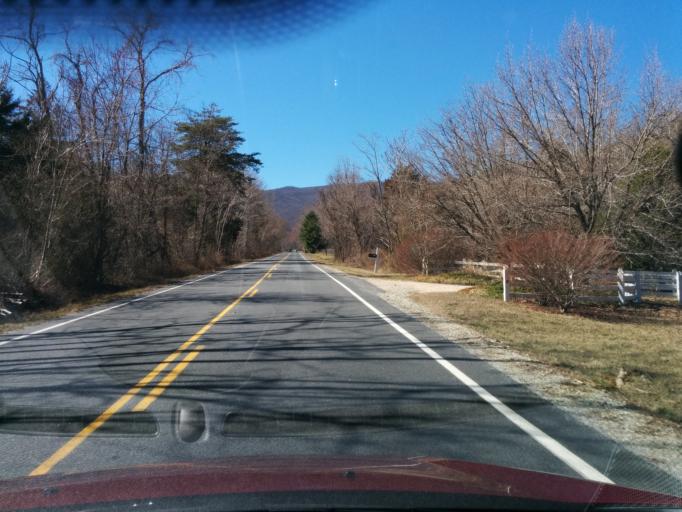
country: US
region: Virginia
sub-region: Nelson County
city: Nellysford
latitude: 37.8770
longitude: -78.9440
